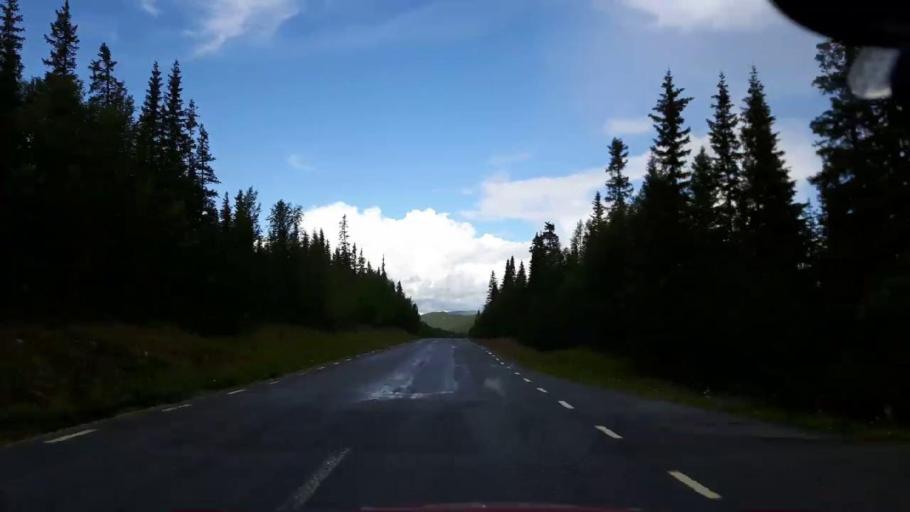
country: SE
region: Vaesterbotten
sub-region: Vilhelmina Kommun
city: Sjoberg
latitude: 65.0040
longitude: 15.1918
